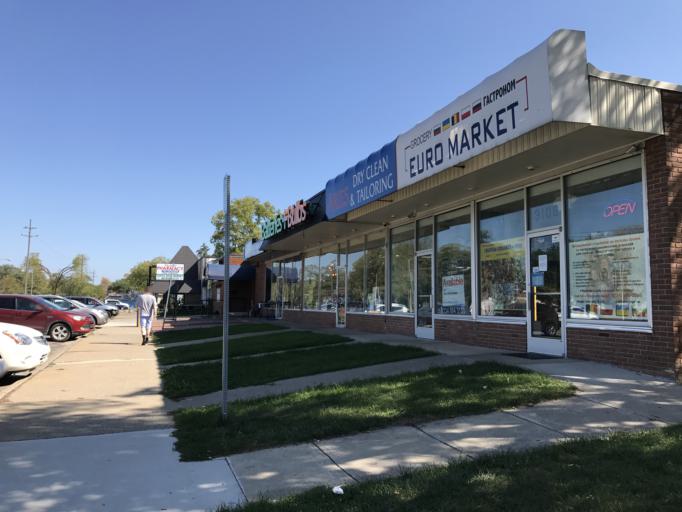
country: US
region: Michigan
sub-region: Washtenaw County
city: Ann Arbor
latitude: 42.2448
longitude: -83.6979
